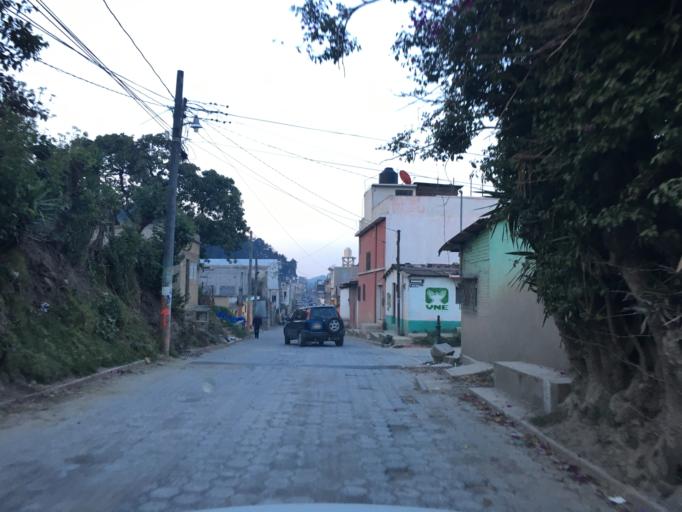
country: GT
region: Chimaltenango
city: Tecpan Guatemala
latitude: 14.7592
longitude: -90.9990
